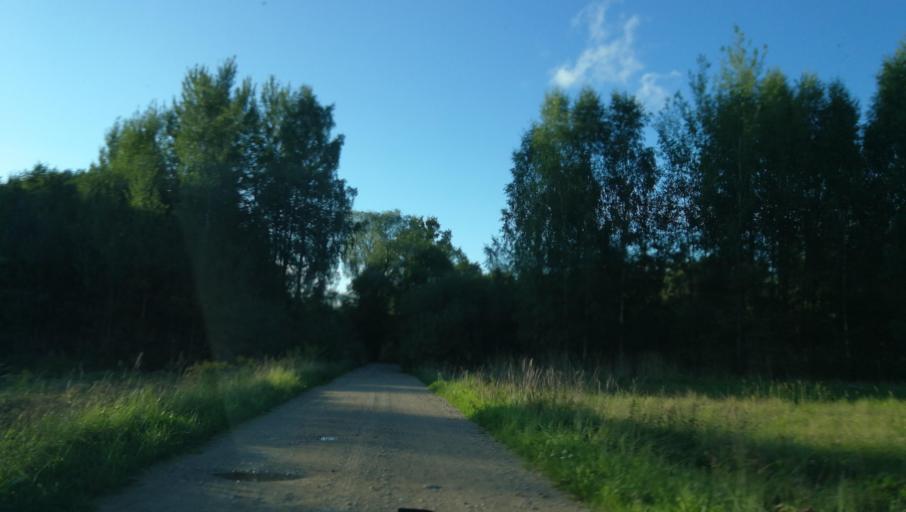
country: LV
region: Valmieras Rajons
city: Valmiera
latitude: 57.5117
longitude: 25.4438
